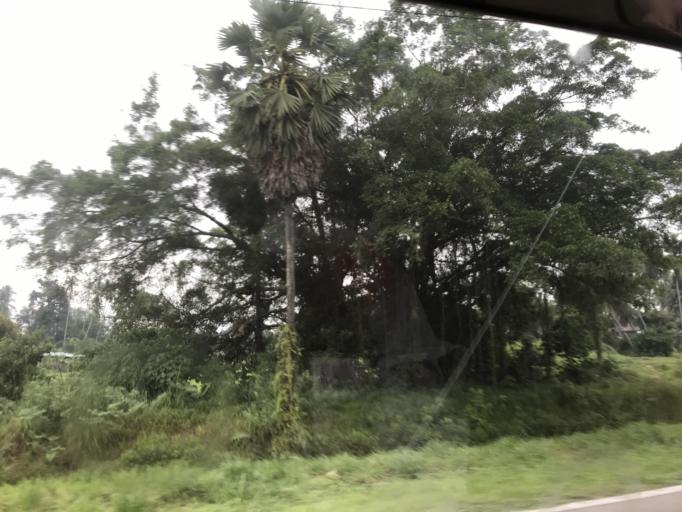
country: MY
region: Kelantan
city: Kota Bharu
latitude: 6.1754
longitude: 102.2245
